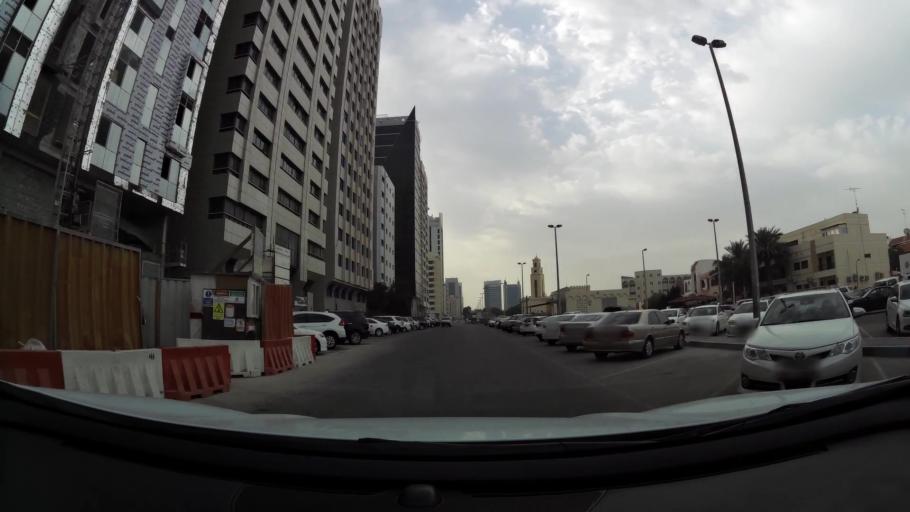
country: AE
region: Abu Dhabi
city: Abu Dhabi
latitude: 24.4660
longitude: 54.3735
